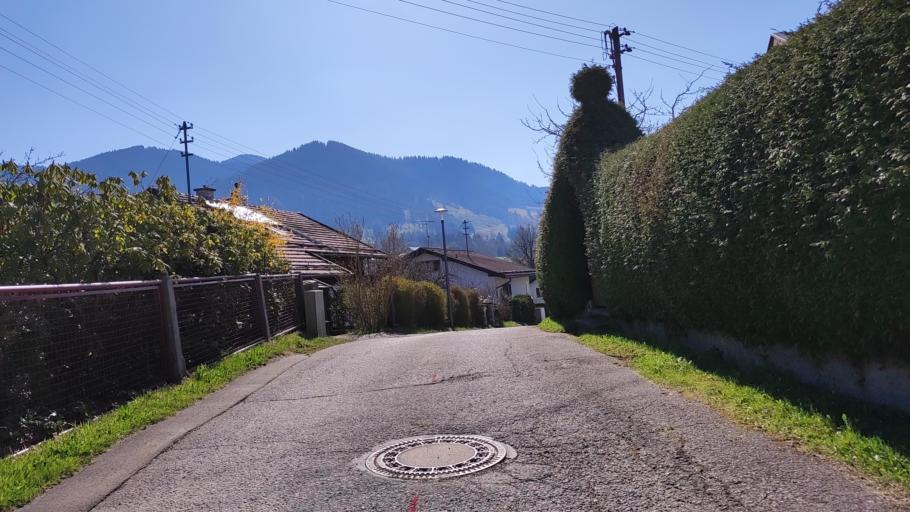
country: DE
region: Bavaria
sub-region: Upper Bavaria
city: Saulgrub
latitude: 47.6463
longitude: 11.0195
